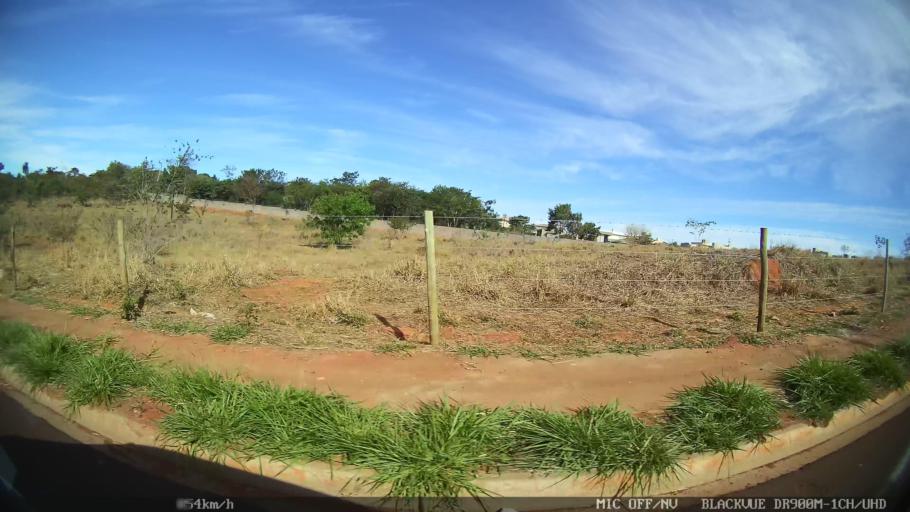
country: BR
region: Sao Paulo
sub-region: Sao Jose Do Rio Preto
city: Sao Jose do Rio Preto
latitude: -20.8055
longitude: -49.3255
